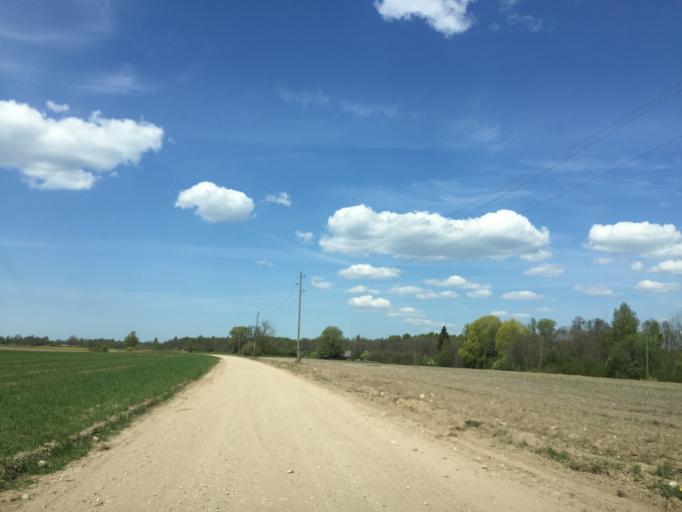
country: LV
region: Limbazu Rajons
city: Limbazi
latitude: 57.3738
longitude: 24.6318
